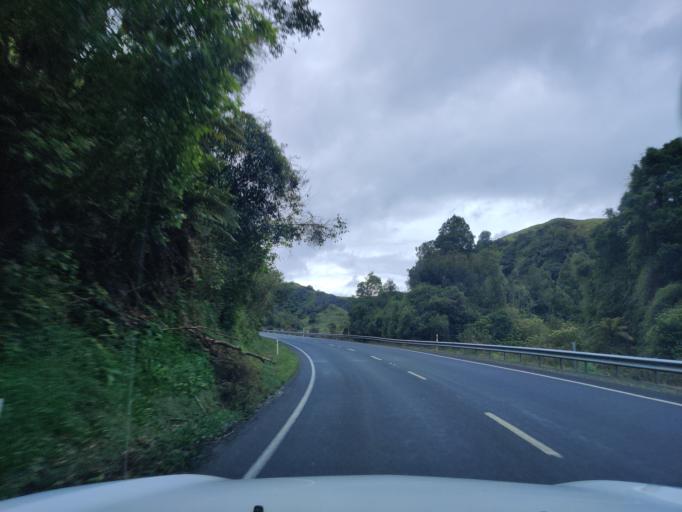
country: NZ
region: Waikato
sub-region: Otorohanga District
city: Otorohanga
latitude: -38.5179
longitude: 175.2067
